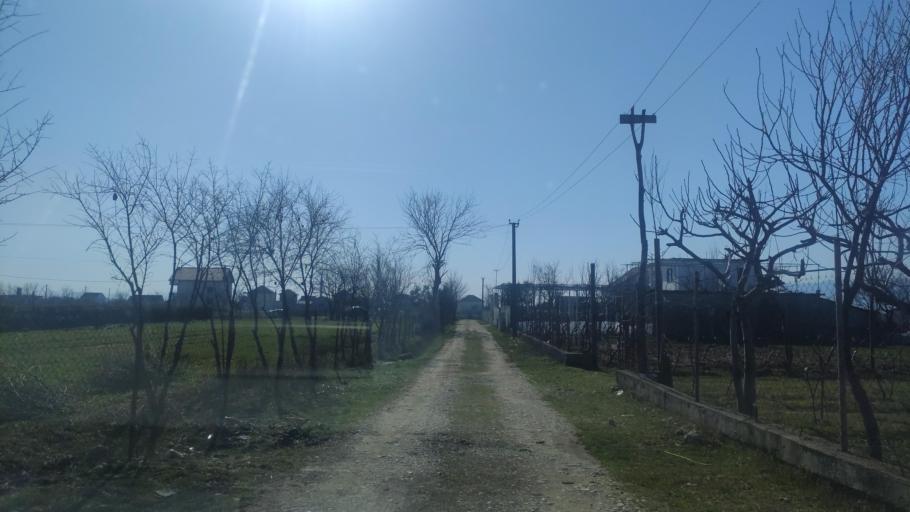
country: AL
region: Shkoder
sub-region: Rrethi i Malesia e Madhe
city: Grude-Fushe
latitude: 42.1654
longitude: 19.4578
